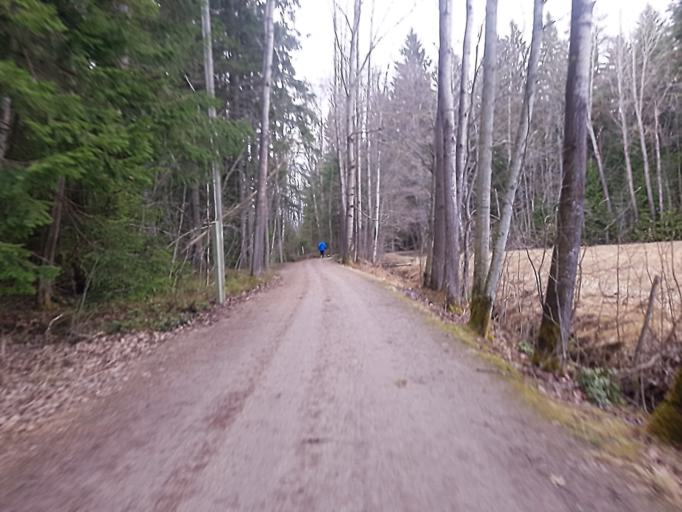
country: FI
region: Uusimaa
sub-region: Helsinki
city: Helsinki
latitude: 60.2685
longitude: 24.9347
